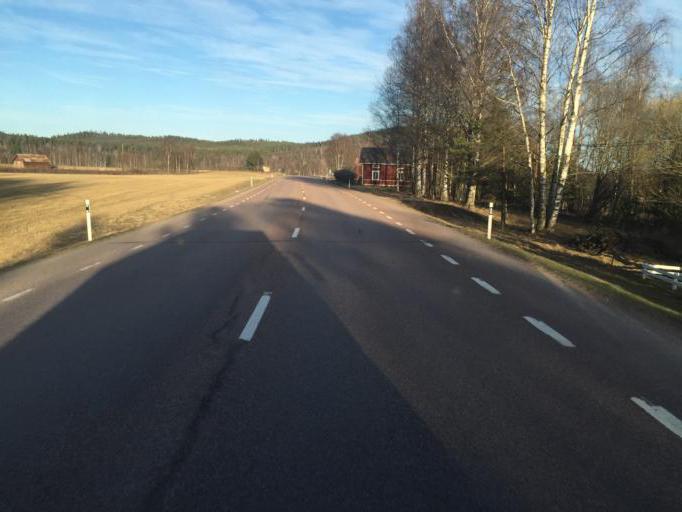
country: SE
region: Dalarna
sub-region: Gagnefs Kommun
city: Djuras
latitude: 60.5516
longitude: 15.2575
